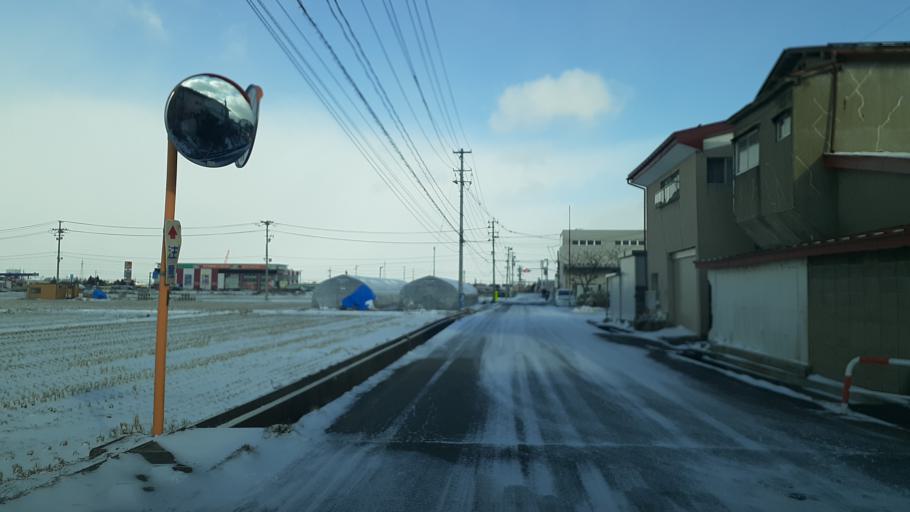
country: JP
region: Fukushima
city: Kitakata
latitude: 37.5156
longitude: 139.9243
